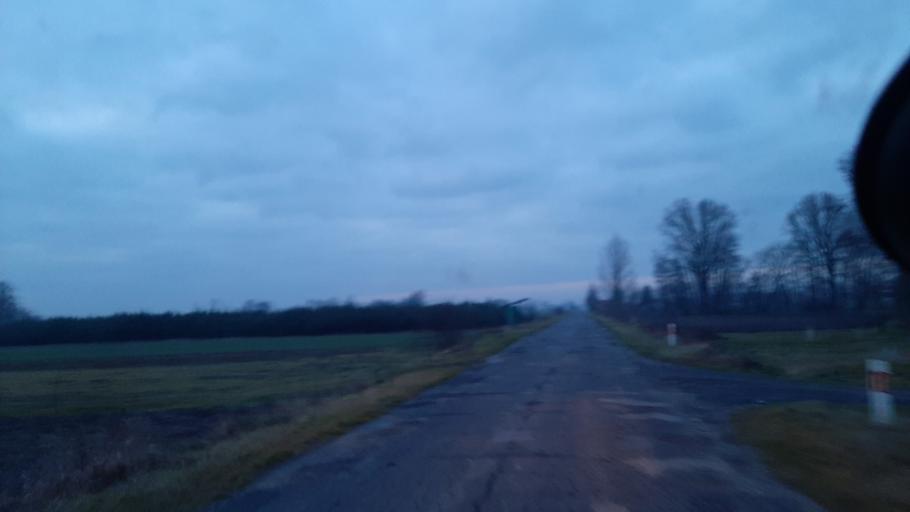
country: PL
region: Lublin Voivodeship
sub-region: Powiat lubartowski
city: Firlej
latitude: 51.6056
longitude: 22.5019
